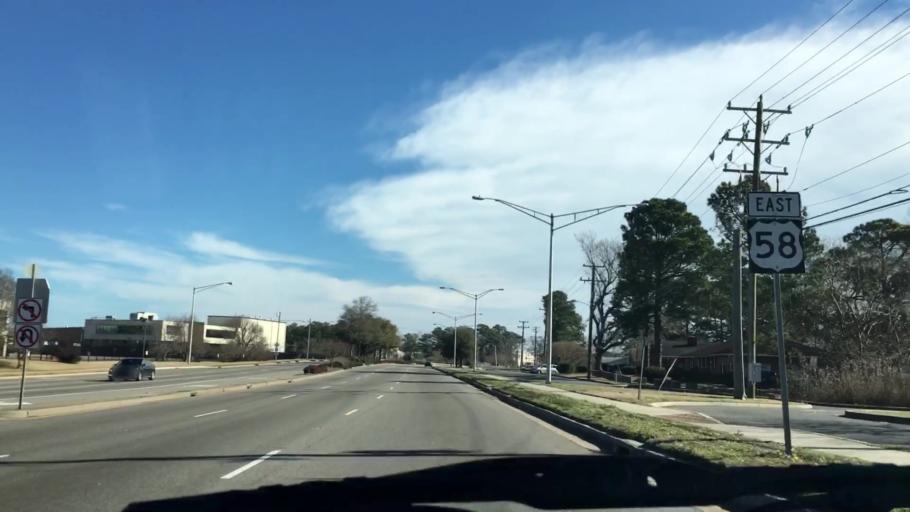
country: US
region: Virginia
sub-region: City of Norfolk
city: Norfolk
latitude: 36.8559
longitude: -76.2318
